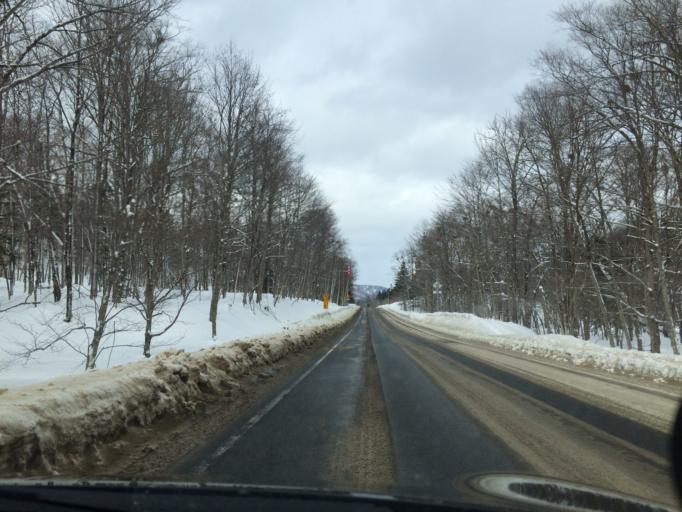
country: JP
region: Hokkaido
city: Shimo-furano
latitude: 42.9212
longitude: 142.3746
